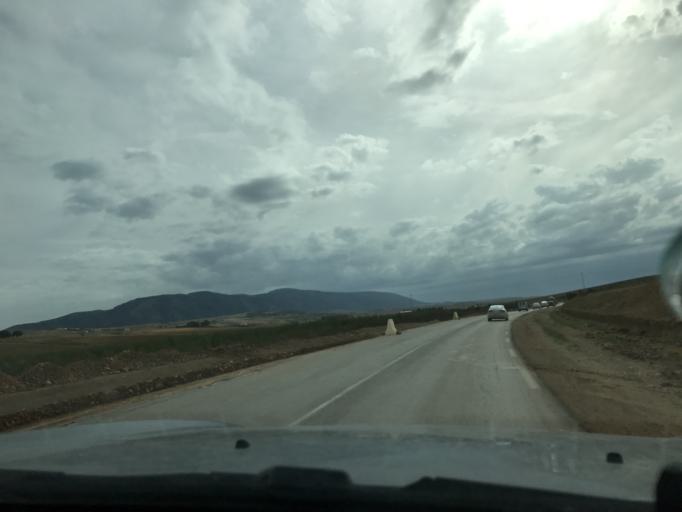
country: TN
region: Silyanah
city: Bu `Aradah
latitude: 36.1545
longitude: 9.6371
